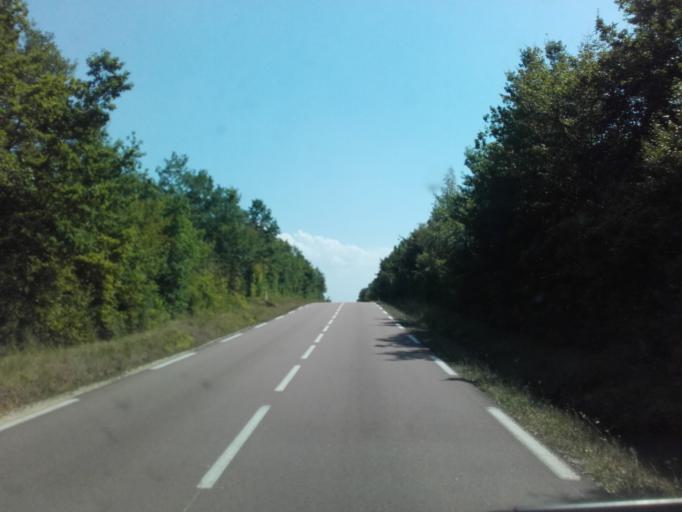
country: FR
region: Bourgogne
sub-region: Departement de l'Yonne
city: Joux-la-Ville
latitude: 47.7055
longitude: 3.8567
